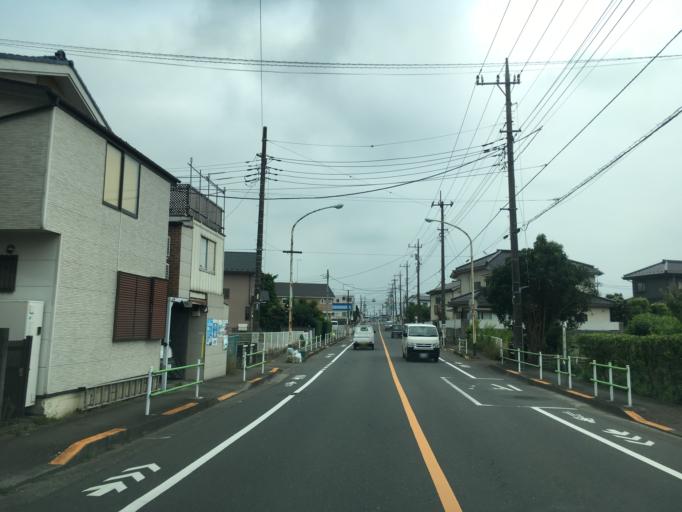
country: JP
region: Tokyo
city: Higashimurayama-shi
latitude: 35.7522
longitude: 139.3986
